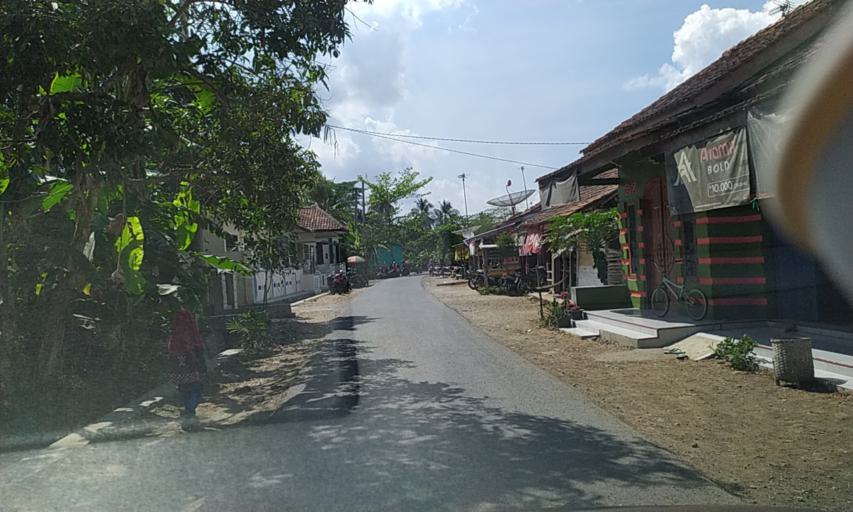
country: ID
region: Central Java
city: Purwodadi
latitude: -7.6151
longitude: 108.7767
